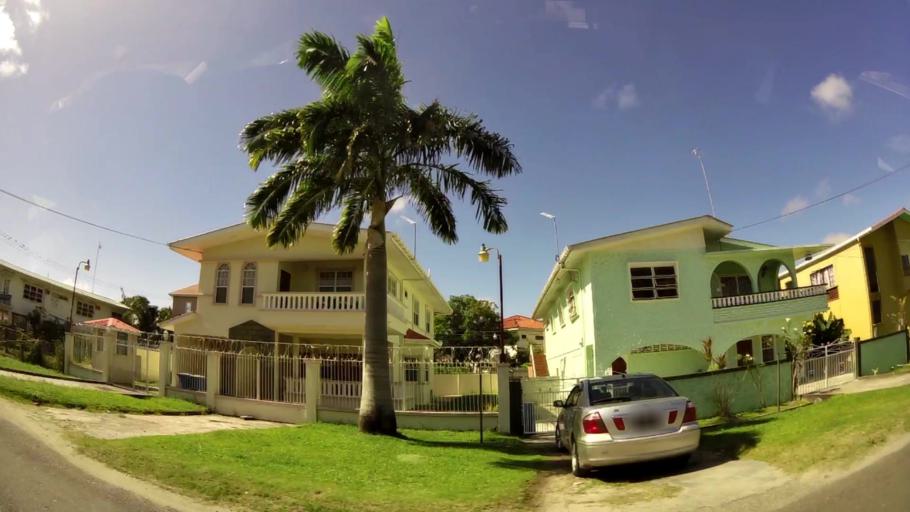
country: GY
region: Demerara-Mahaica
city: Georgetown
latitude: 6.8082
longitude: -58.1336
